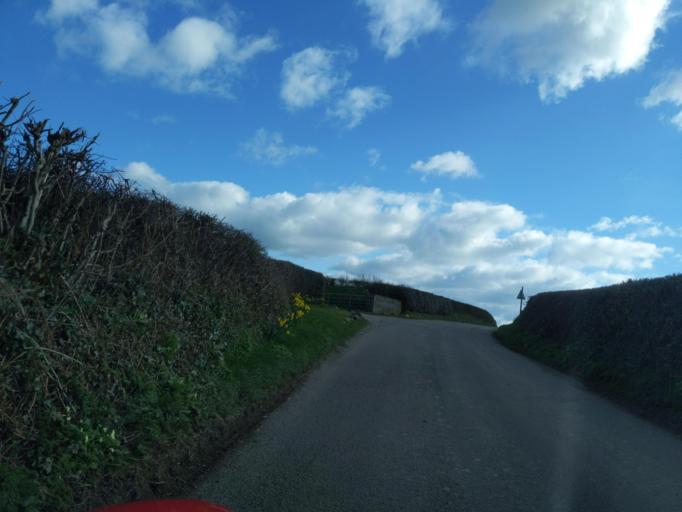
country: GB
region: England
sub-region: Devon
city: Salcombe
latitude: 50.2650
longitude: -3.7192
